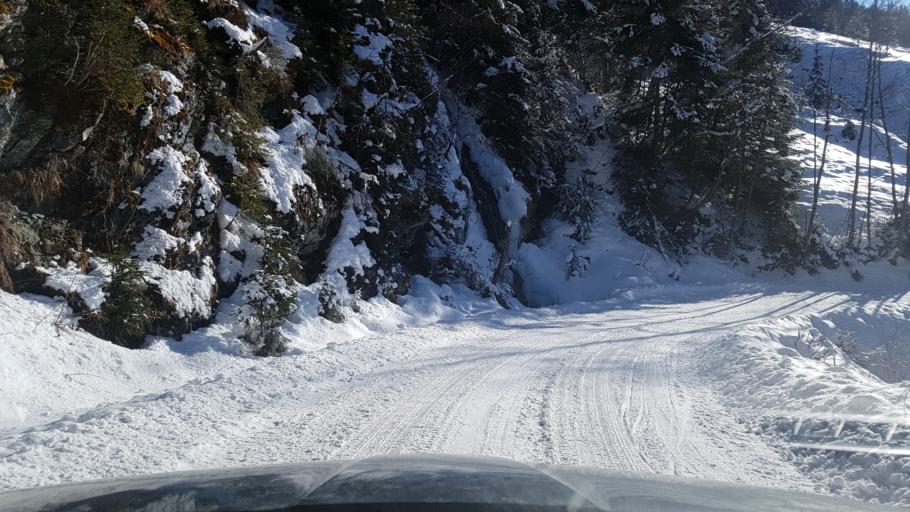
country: AT
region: Salzburg
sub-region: Politischer Bezirk Sankt Johann im Pongau
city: Huttschlag
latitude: 47.1804
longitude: 13.2698
